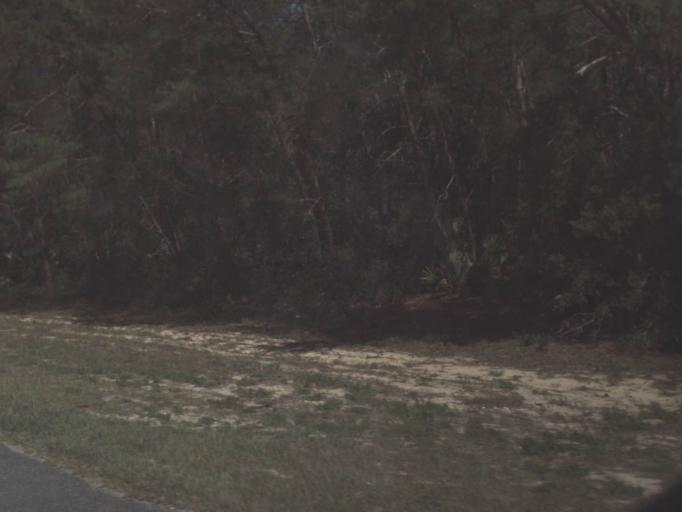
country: US
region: Florida
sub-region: Lake County
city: Astor
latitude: 29.1774
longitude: -81.7676
